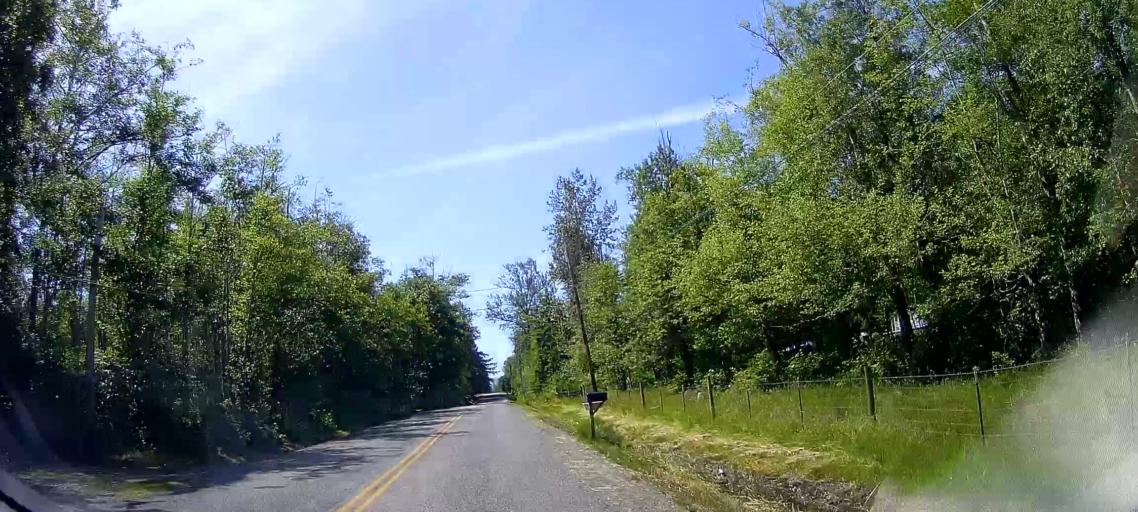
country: US
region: Washington
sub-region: Skagit County
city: Sedro-Woolley
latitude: 48.5343
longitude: -122.2481
